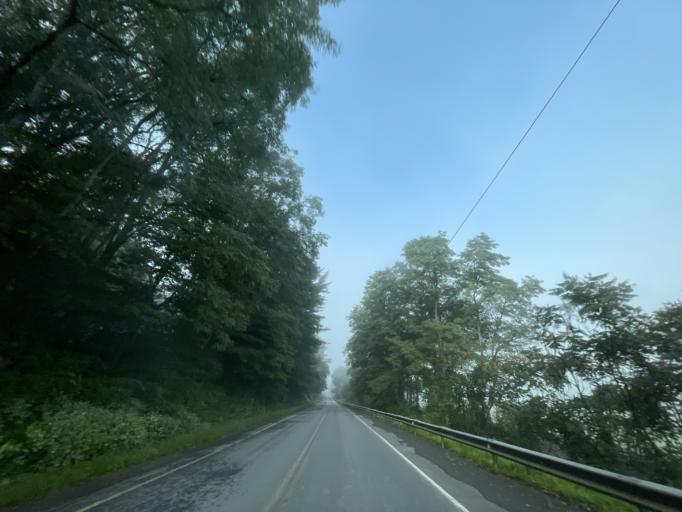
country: US
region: New York
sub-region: Chenango County
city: Oxford
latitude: 42.3676
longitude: -75.6606
